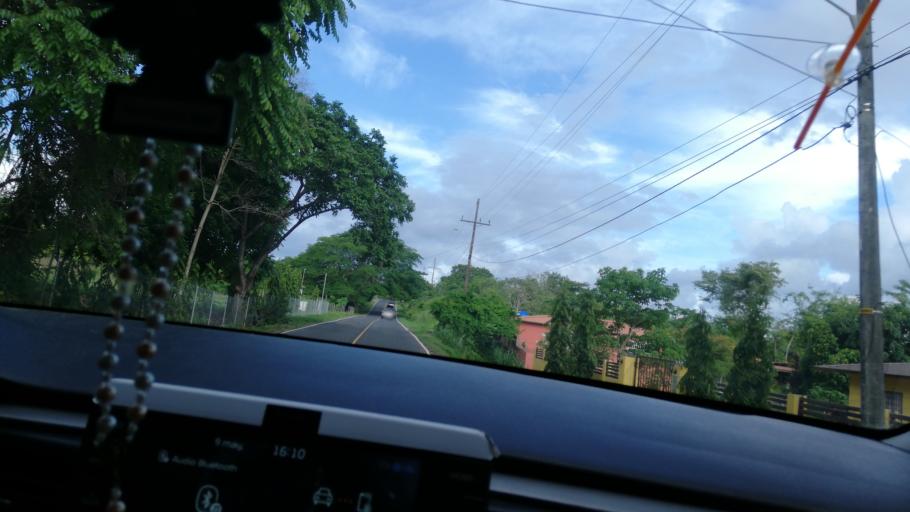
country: PA
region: Panama
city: Las Colinas
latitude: 8.4871
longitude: -80.0219
